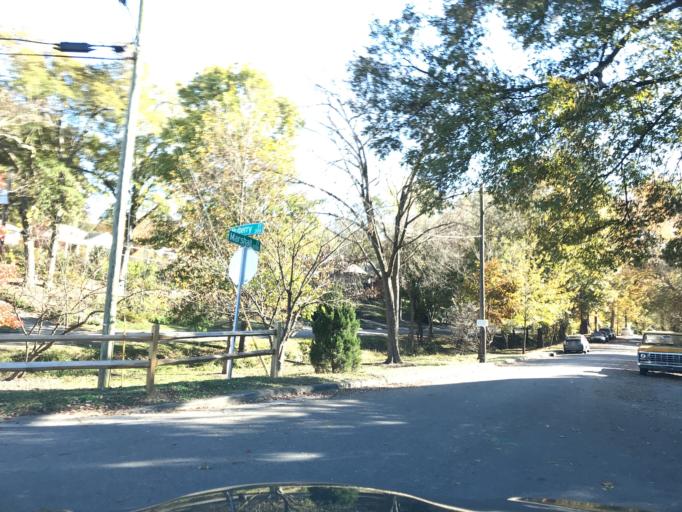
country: US
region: North Carolina
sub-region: Wake County
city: Raleigh
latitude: 35.7977
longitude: -78.6346
